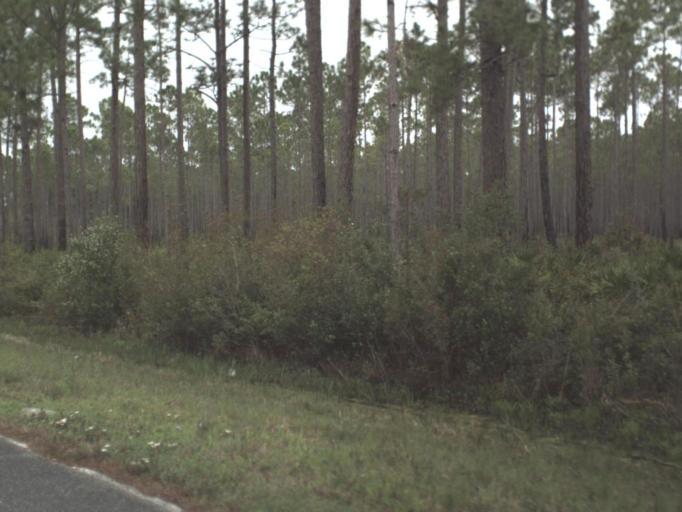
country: US
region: Florida
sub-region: Franklin County
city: Eastpoint
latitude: 29.8166
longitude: -84.8472
